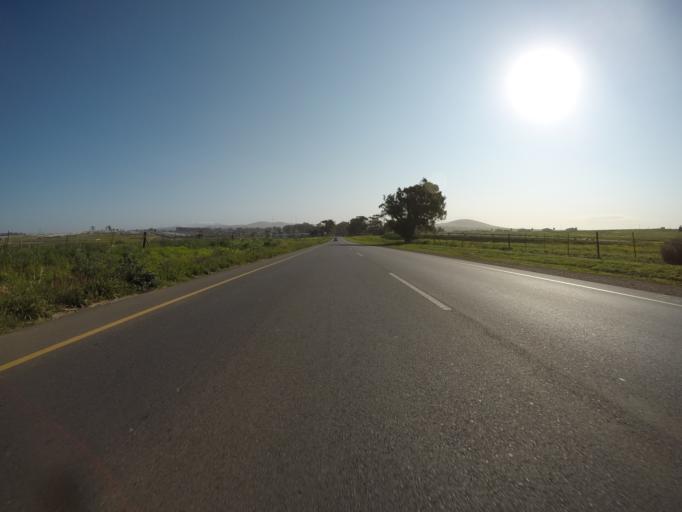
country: ZA
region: Western Cape
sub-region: City of Cape Town
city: Kraaifontein
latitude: -33.7779
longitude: 18.7275
